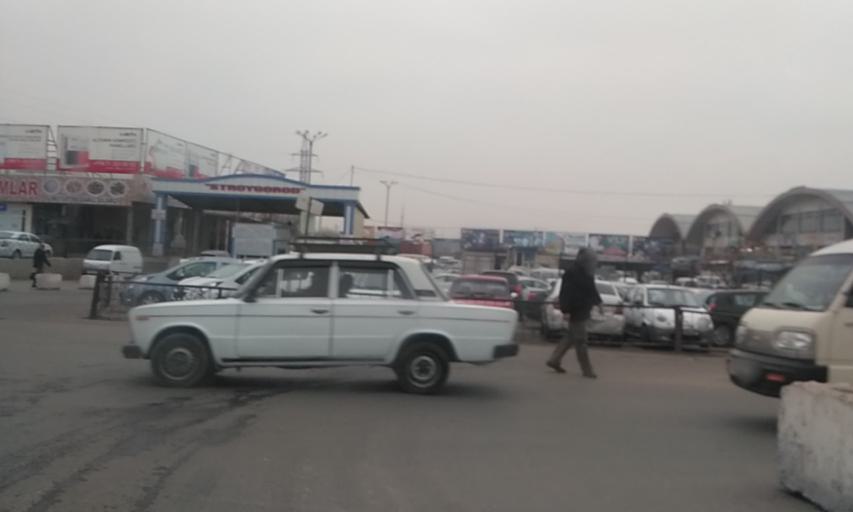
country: UZ
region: Toshkent Shahri
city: Tashkent
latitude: 41.2889
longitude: 69.1498
